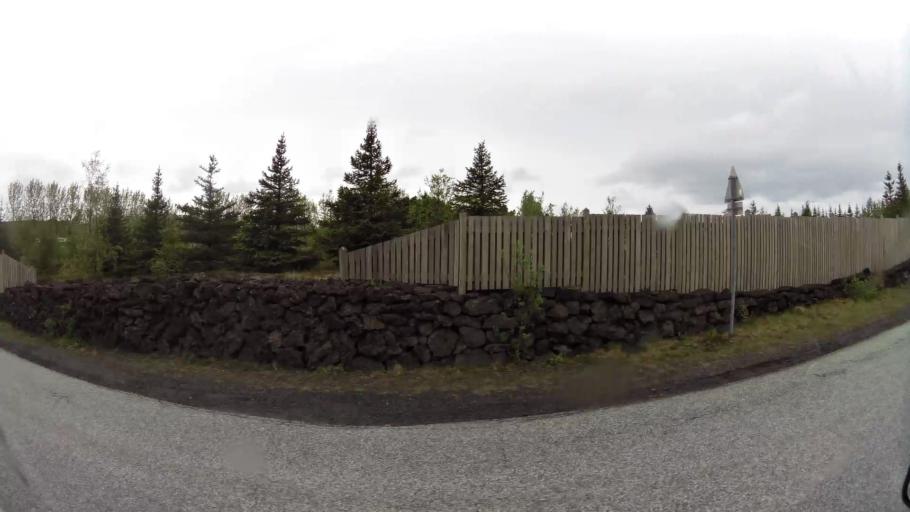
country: IS
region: Capital Region
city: Hafnarfjoerdur
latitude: 64.0643
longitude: -21.9339
